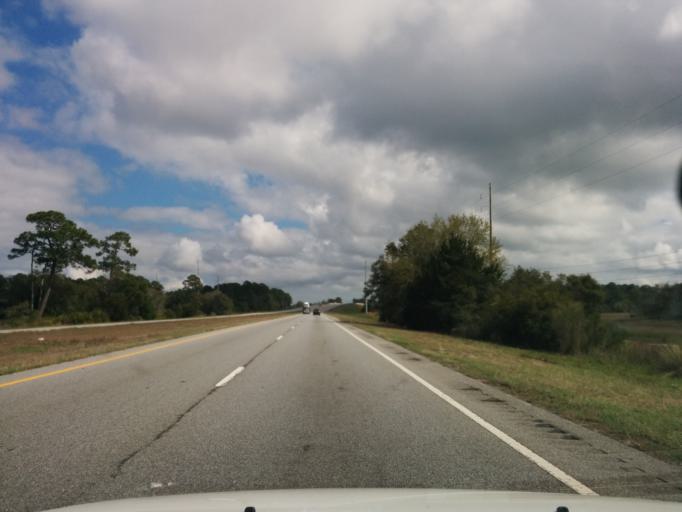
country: US
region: Georgia
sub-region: Glynn County
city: Brunswick
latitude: 31.1249
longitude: -81.5490
